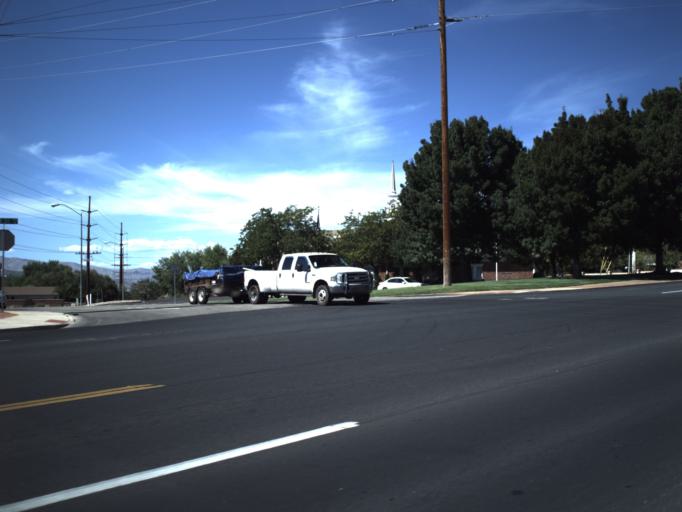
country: US
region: Utah
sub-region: Washington County
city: Saint George
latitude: 37.1286
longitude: -113.6021
